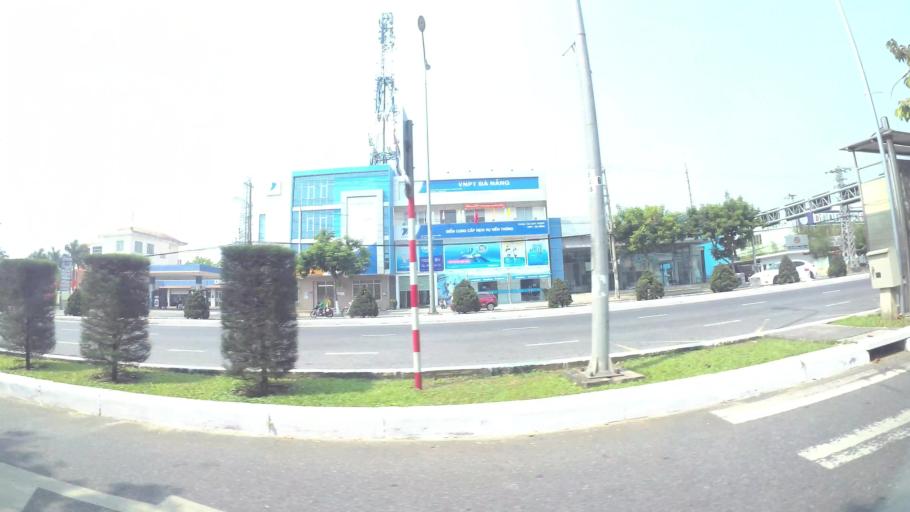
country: VN
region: Da Nang
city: Son Tra
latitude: 16.0399
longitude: 108.2426
